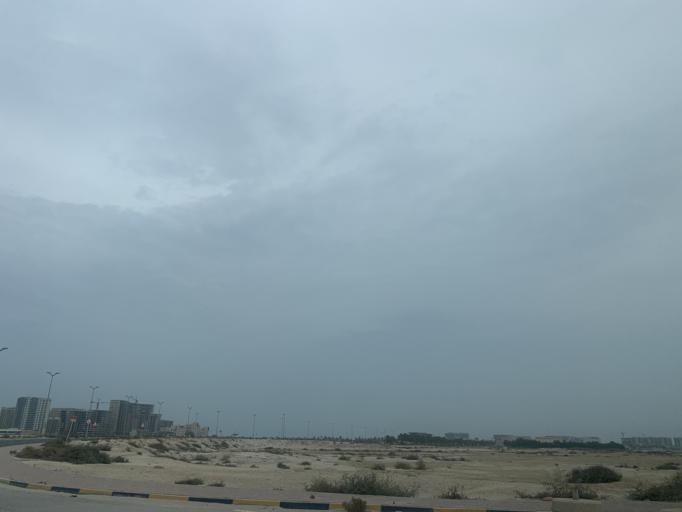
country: BH
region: Muharraq
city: Al Hadd
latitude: 26.2835
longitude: 50.6526
